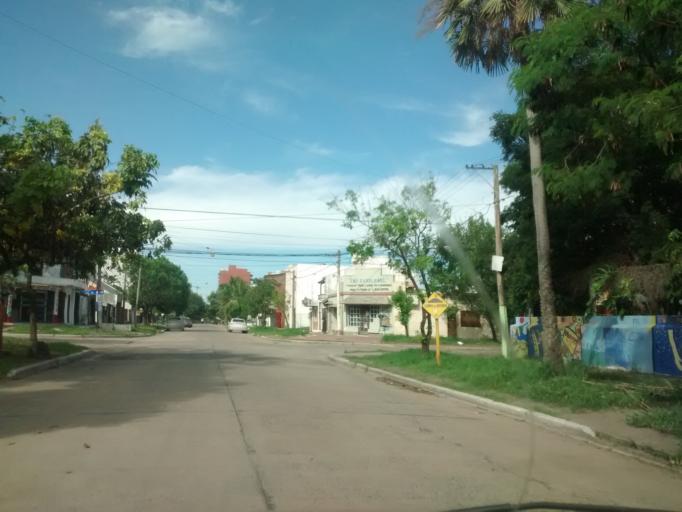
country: AR
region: Chaco
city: Resistencia
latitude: -27.4514
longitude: -58.9991
